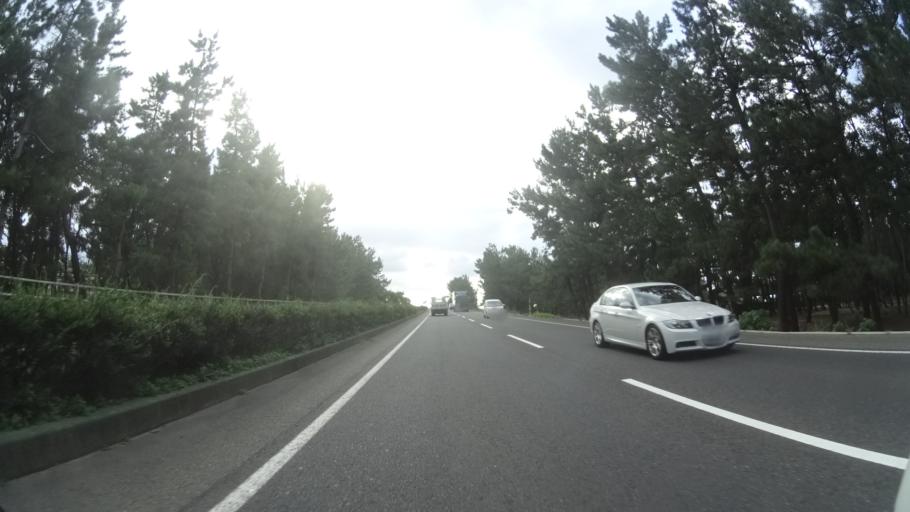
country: JP
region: Tottori
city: Kurayoshi
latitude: 35.4997
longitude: 133.7590
